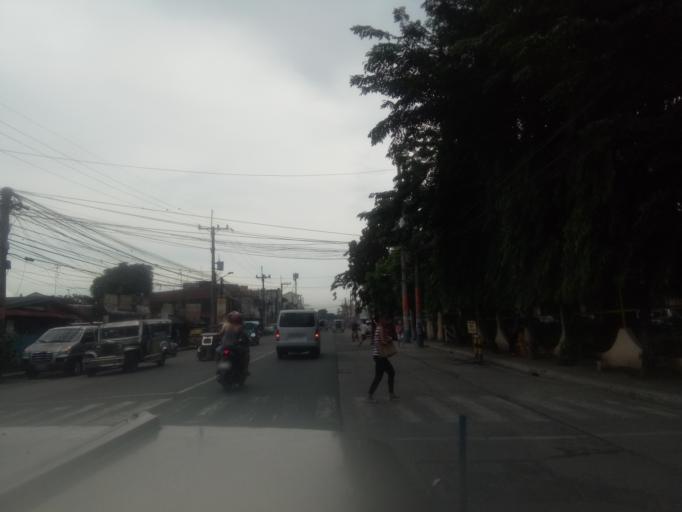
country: PH
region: Calabarzon
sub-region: Province of Cavite
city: Bulihan
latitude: 14.2957
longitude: 121.0073
